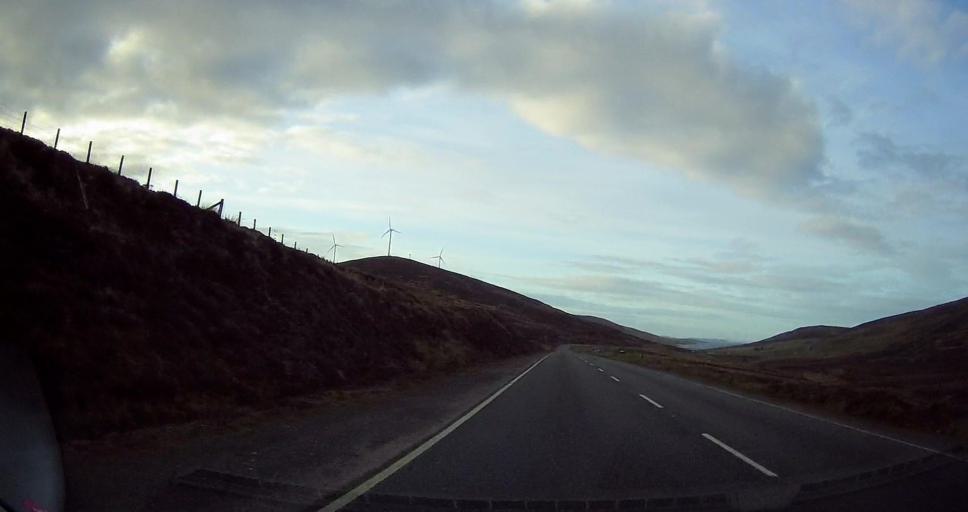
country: GB
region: Scotland
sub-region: Shetland Islands
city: Lerwick
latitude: 60.1522
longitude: -1.2366
